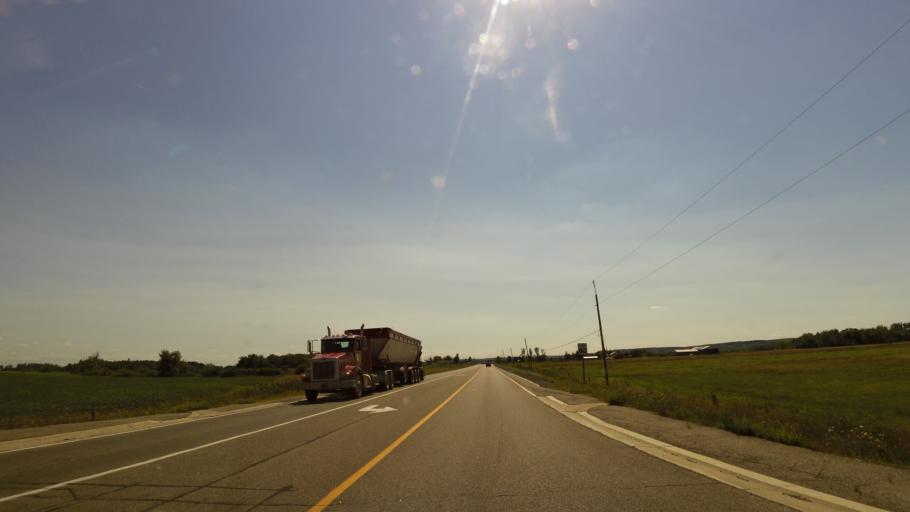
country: CA
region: Ontario
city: Brampton
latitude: 43.7637
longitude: -79.8891
